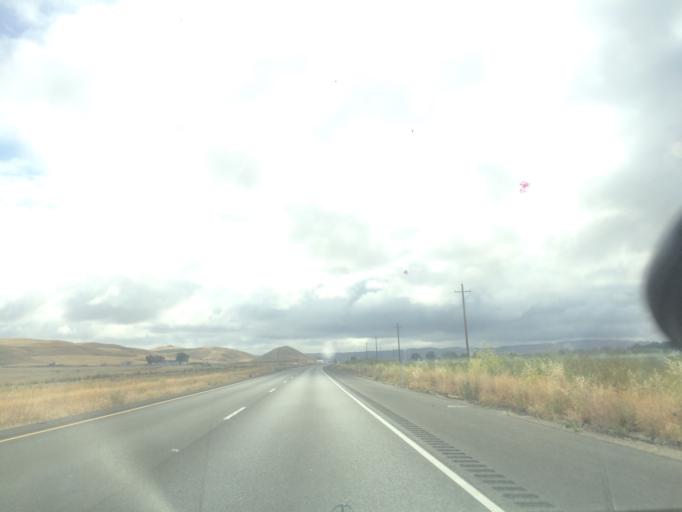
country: US
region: California
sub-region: San Luis Obispo County
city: Shandon
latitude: 35.6612
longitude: -120.4371
